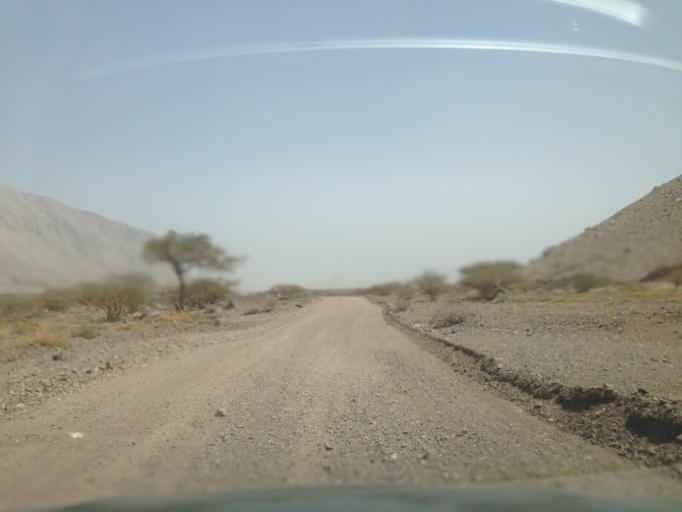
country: OM
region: Az Zahirah
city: `Ibri
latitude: 23.1819
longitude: 56.8987
